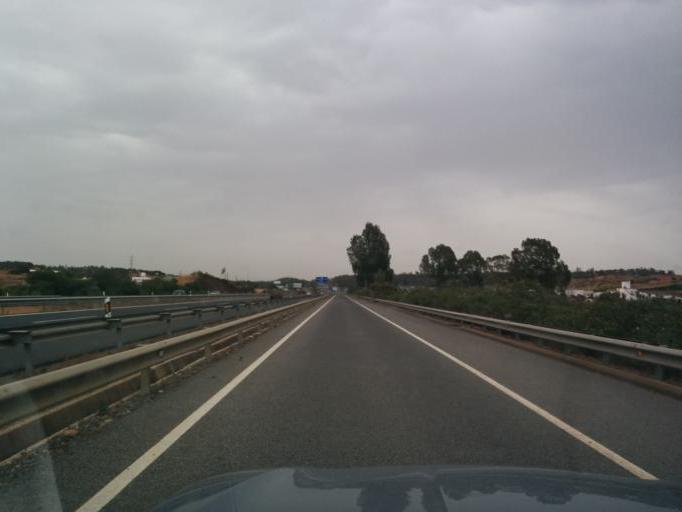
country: ES
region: Andalusia
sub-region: Provincia de Huelva
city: Ayamonte
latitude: 37.2385
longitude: -7.3920
